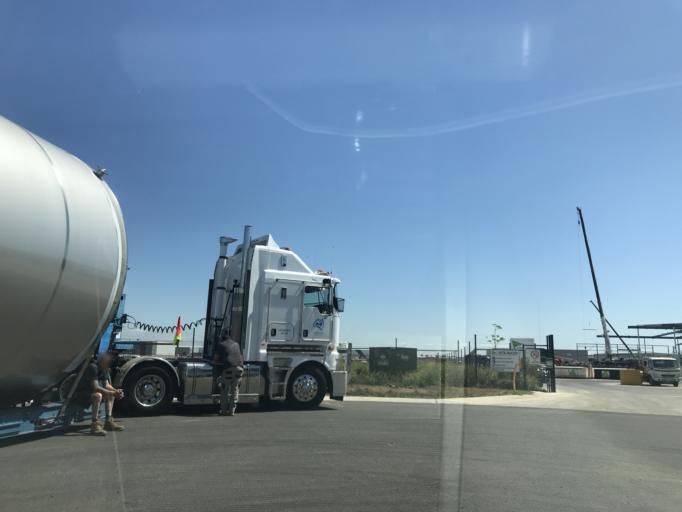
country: AU
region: Victoria
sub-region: Wyndham
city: Truganina
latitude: -37.8304
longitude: 144.7677
